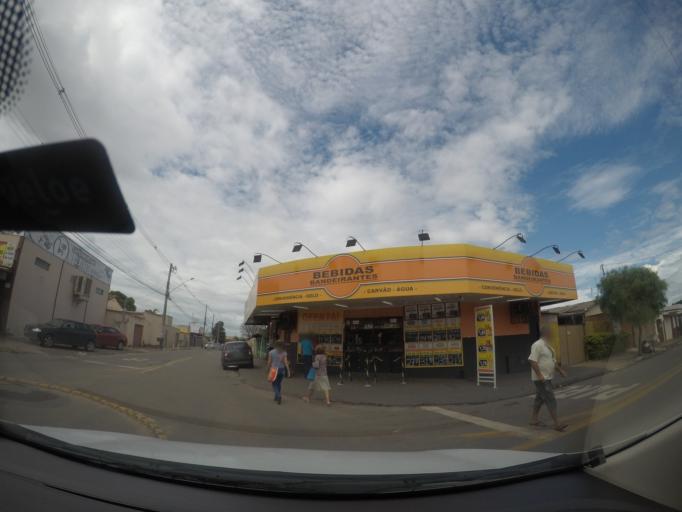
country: BR
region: Goias
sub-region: Aparecida De Goiania
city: Aparecida de Goiania
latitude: -16.7597
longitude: -49.3504
